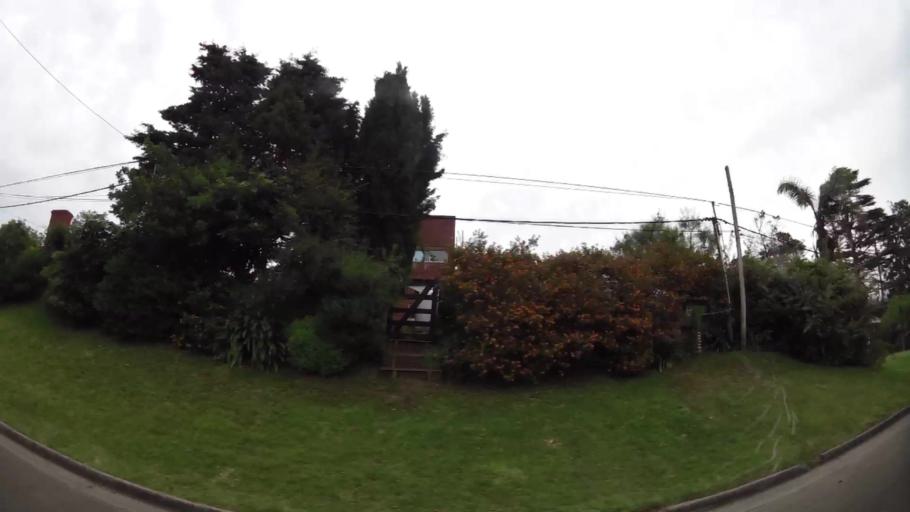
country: UY
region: Maldonado
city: Maldonado
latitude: -34.9155
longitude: -54.9729
